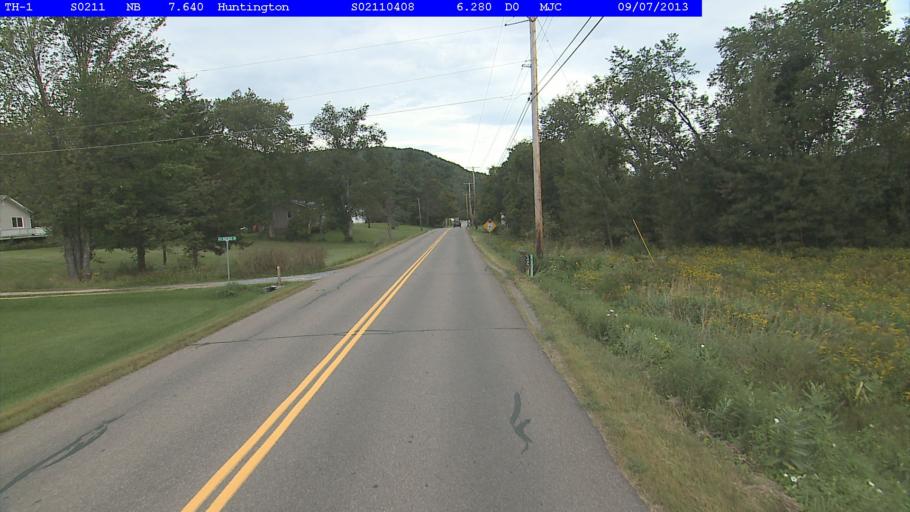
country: US
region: Vermont
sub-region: Chittenden County
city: Hinesburg
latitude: 44.3098
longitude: -72.9859
